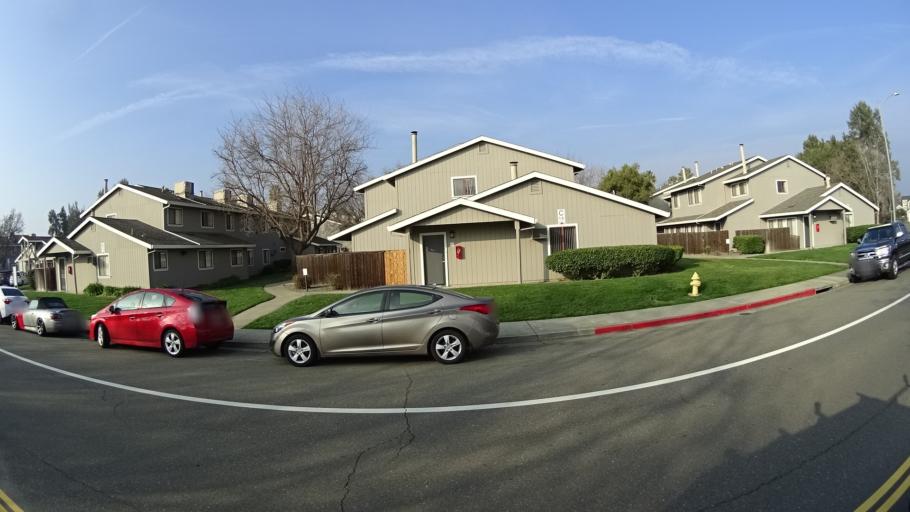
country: US
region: California
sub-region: Yolo County
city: Davis
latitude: 38.5662
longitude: -121.7655
